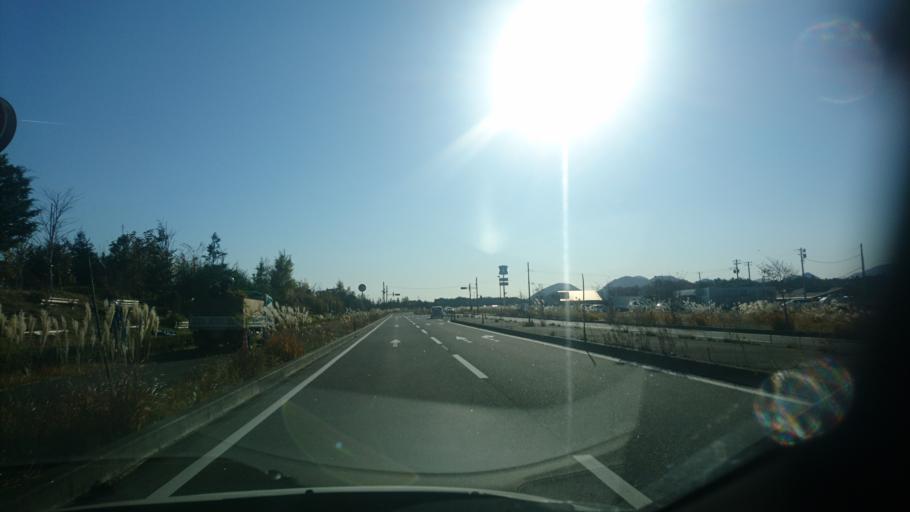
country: JP
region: Miyagi
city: Tomiya
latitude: 38.4715
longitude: 140.8920
